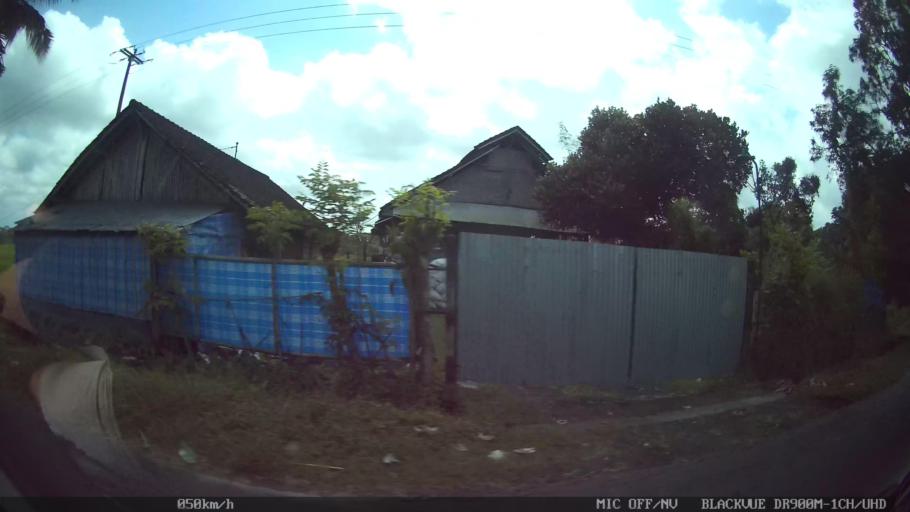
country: ID
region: Bali
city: Banjar Mulung
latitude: -8.5024
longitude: 115.3218
